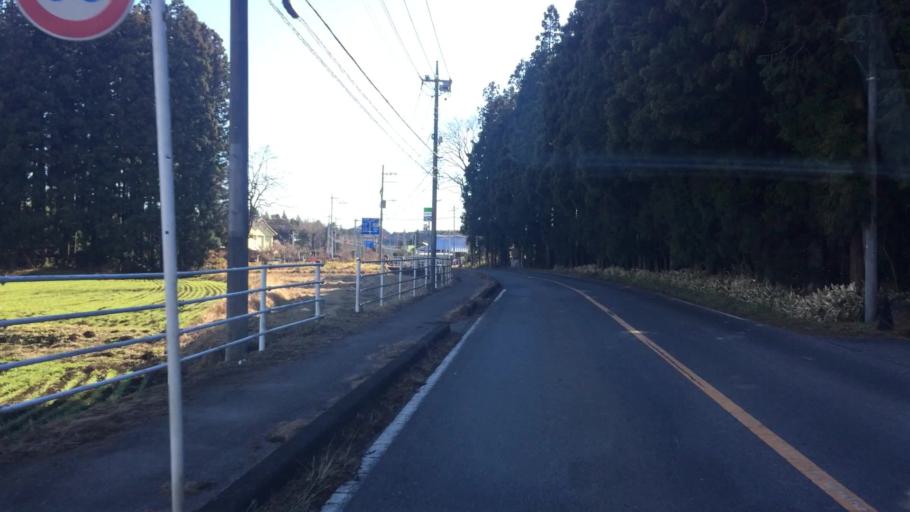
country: JP
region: Tochigi
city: Imaichi
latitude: 36.7507
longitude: 139.7340
